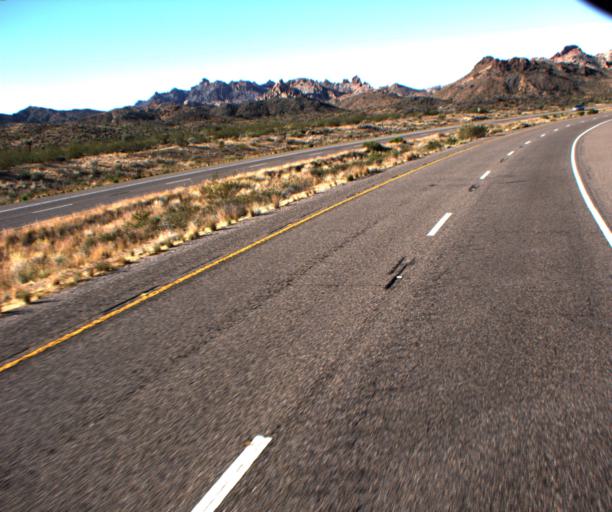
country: US
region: Nevada
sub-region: Clark County
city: Laughlin
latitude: 35.1970
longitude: -114.4049
